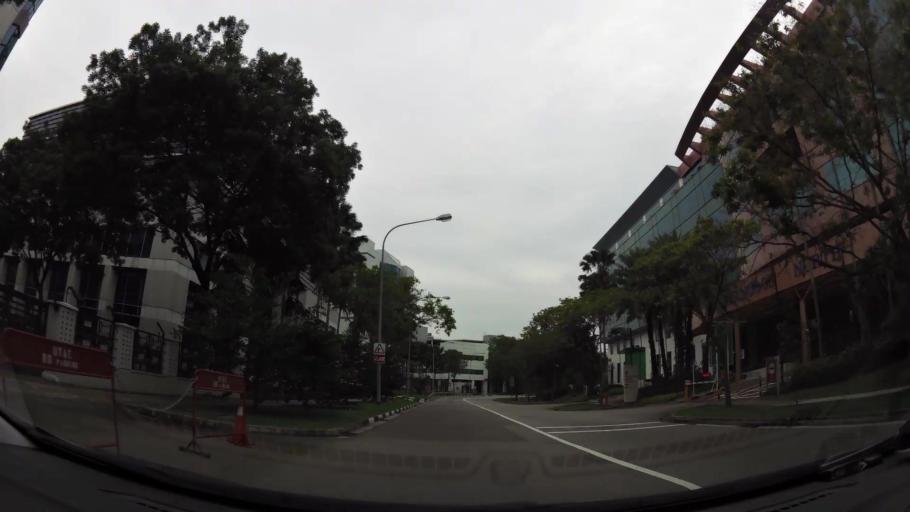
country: SG
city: Singapore
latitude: 1.3743
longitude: 103.8684
